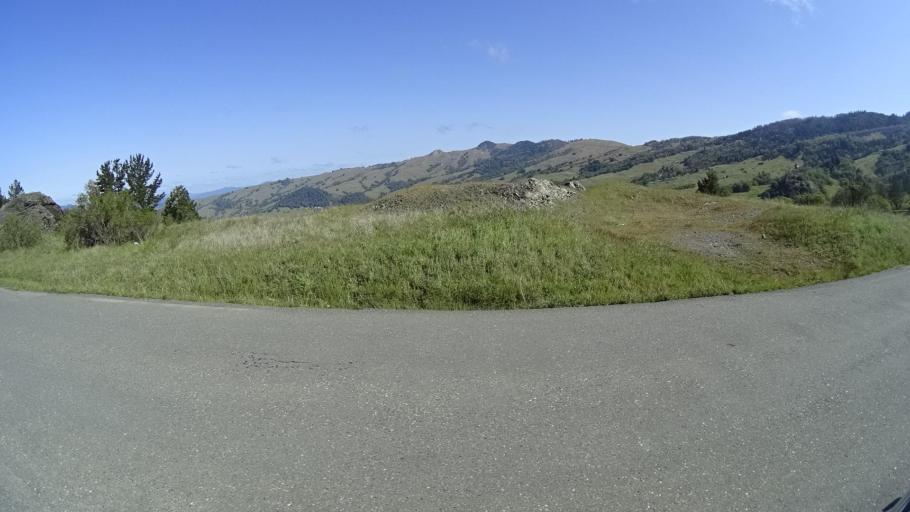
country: US
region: California
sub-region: Humboldt County
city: Redway
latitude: 40.1121
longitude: -123.7233
